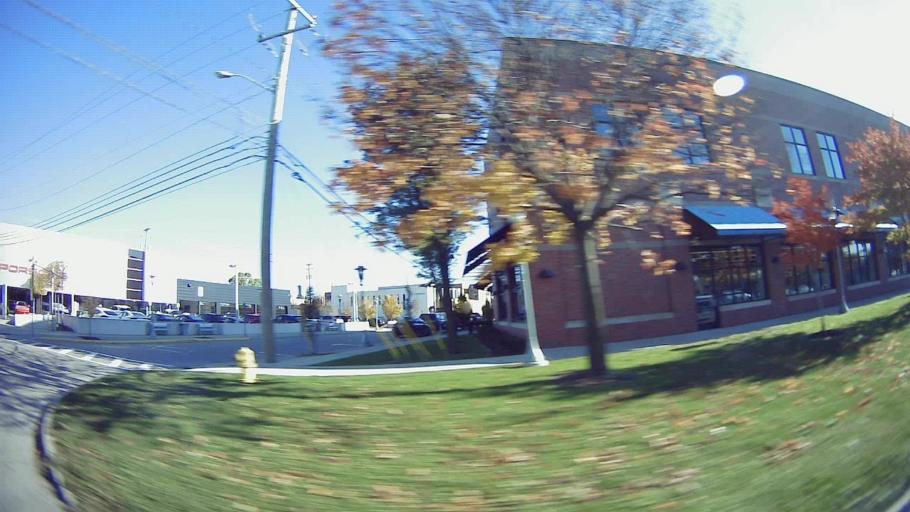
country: US
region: Michigan
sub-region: Oakland County
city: Birmingham
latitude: 42.5421
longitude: -83.2086
